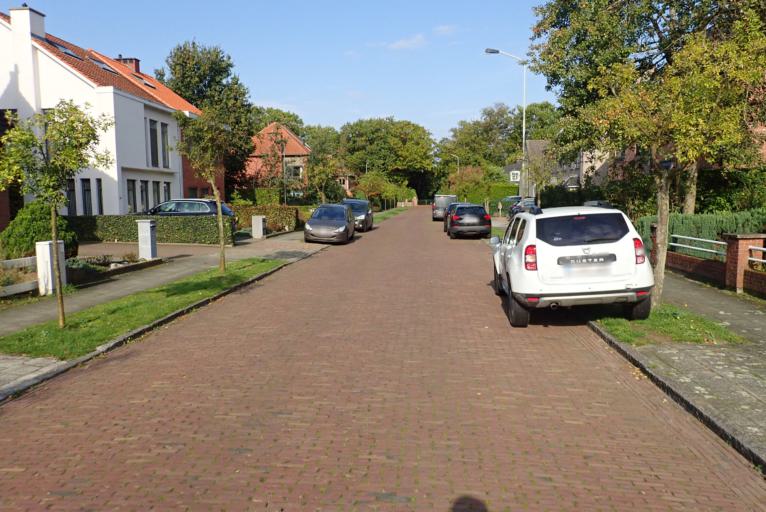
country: BE
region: Flanders
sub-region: Provincie Antwerpen
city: Kapellen
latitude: 51.3093
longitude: 4.4361
